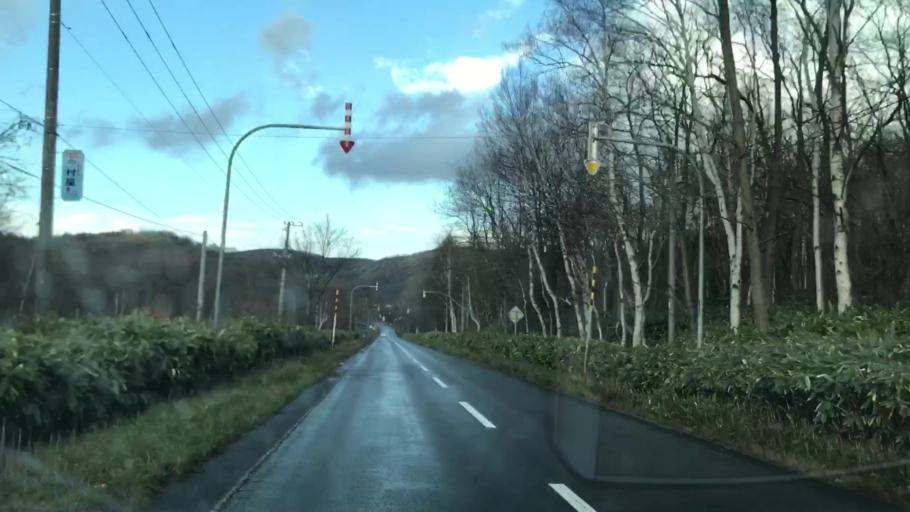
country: JP
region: Hokkaido
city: Yoichi
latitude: 43.3224
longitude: 140.5158
